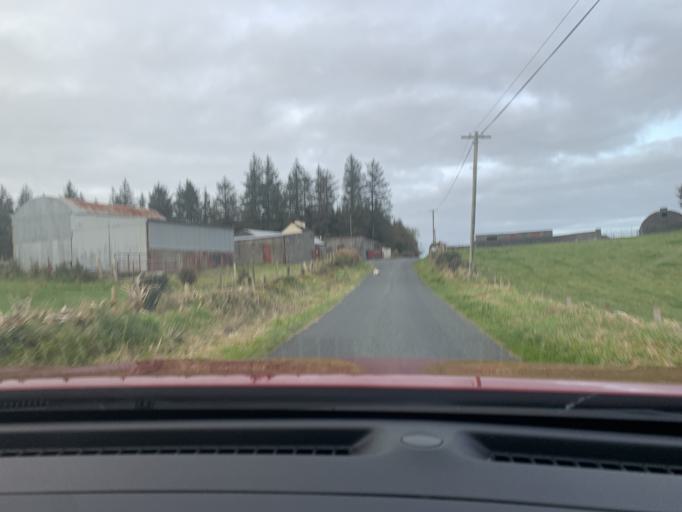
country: IE
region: Connaught
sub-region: Sligo
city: Tobercurry
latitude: 54.0617
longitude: -8.6844
